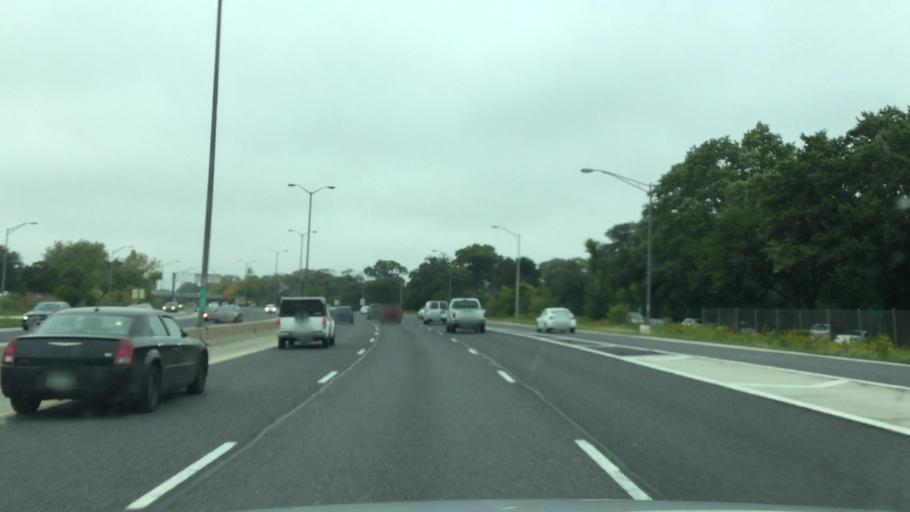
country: US
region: Illinois
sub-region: Cook County
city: Wilmette
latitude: 42.0645
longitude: -87.7547
